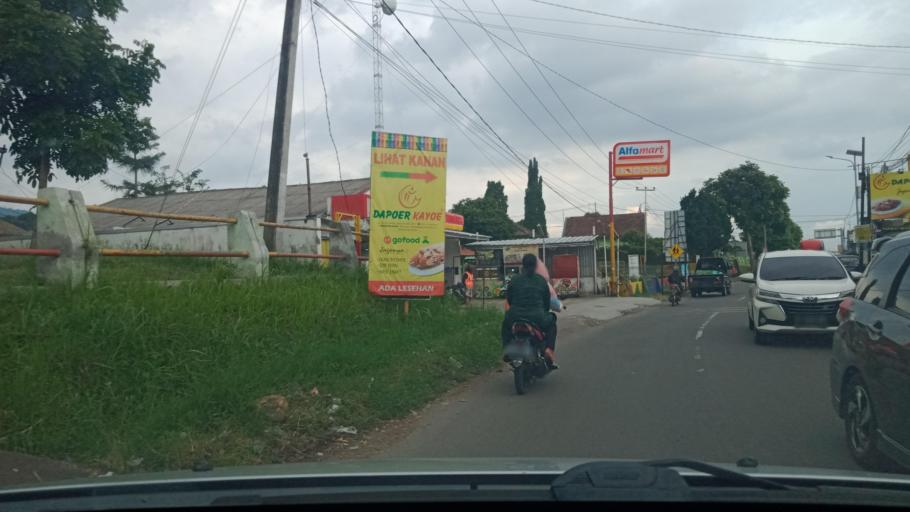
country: ID
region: West Java
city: Lembang
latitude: -6.8029
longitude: 107.5829
